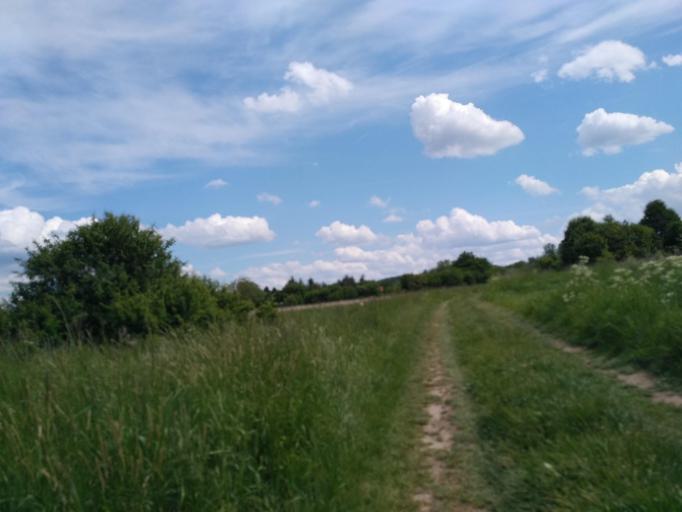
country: PL
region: Subcarpathian Voivodeship
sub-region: Powiat krosnienski
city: Odrzykon
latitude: 49.7174
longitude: 21.7508
